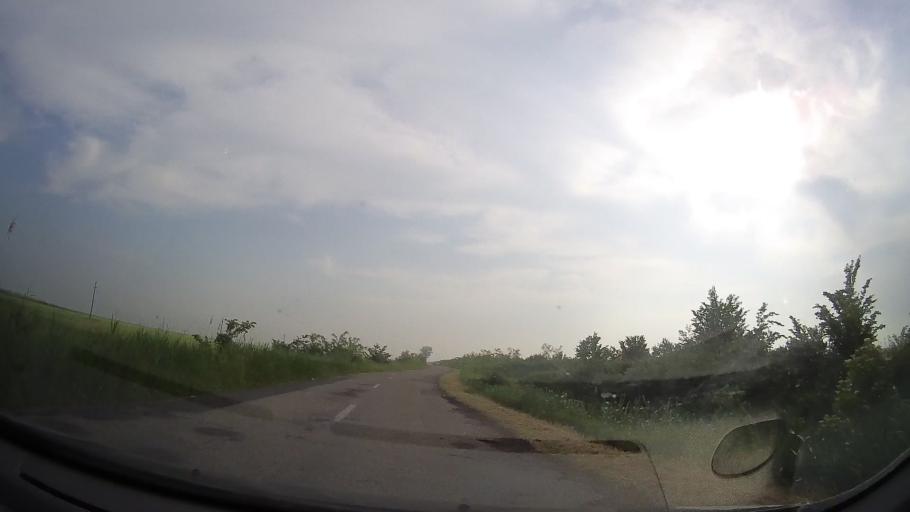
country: RO
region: Timis
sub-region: Comuna Peciu Nou
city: Peciu Nou
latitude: 45.5802
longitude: 21.0228
